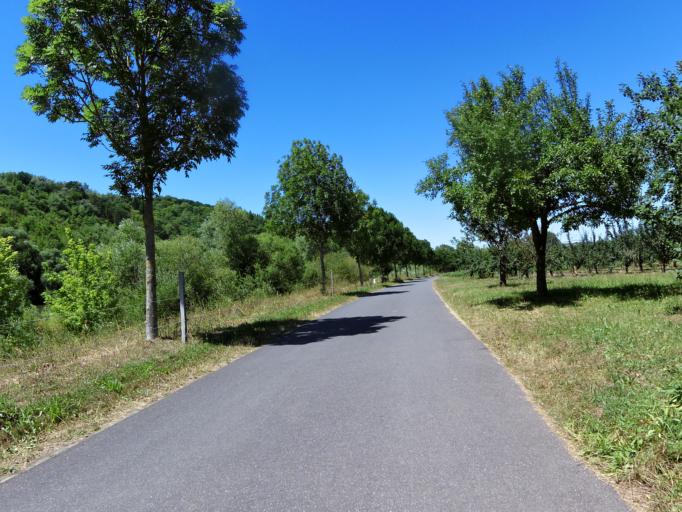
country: DE
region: Bavaria
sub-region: Regierungsbezirk Unterfranken
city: Sommerhausen
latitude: 49.6909
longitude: 10.0228
